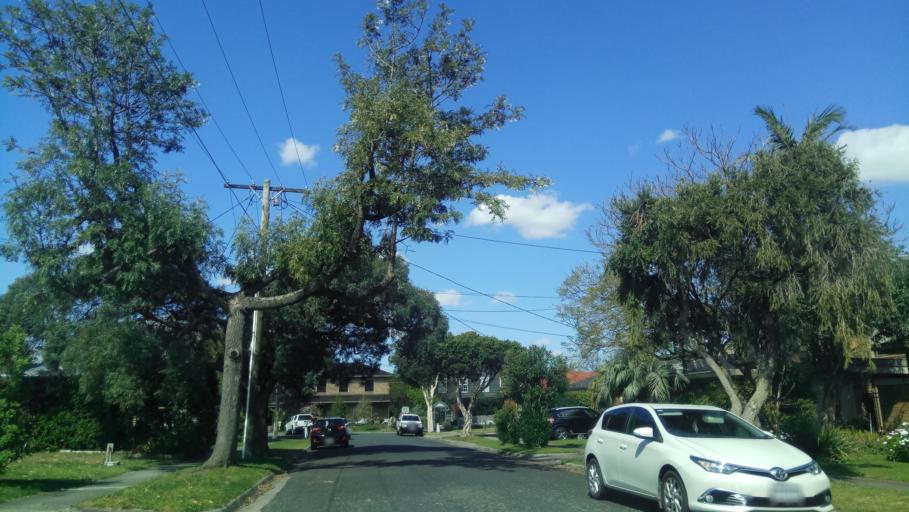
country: AU
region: Victoria
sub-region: Kingston
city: Dingley Village
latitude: -37.9798
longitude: 145.1250
